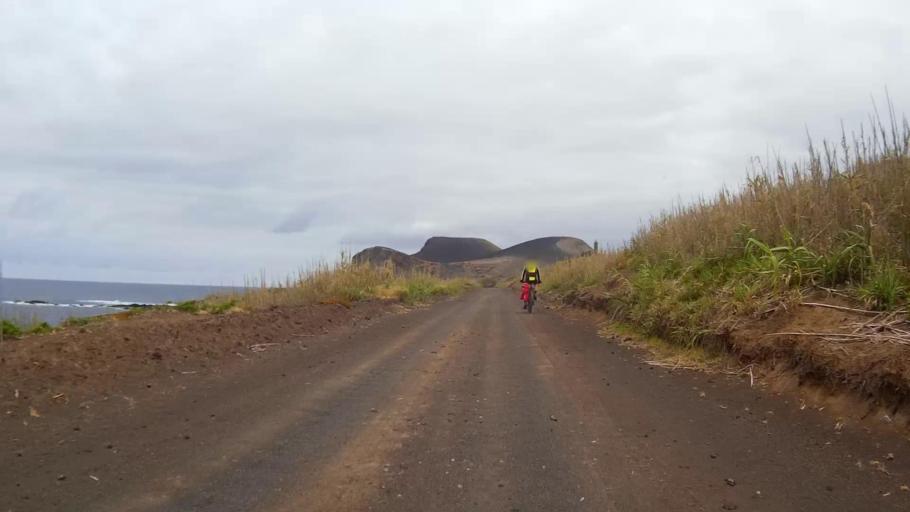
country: PT
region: Azores
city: Ribeira Grande
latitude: 38.5894
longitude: -28.8228
